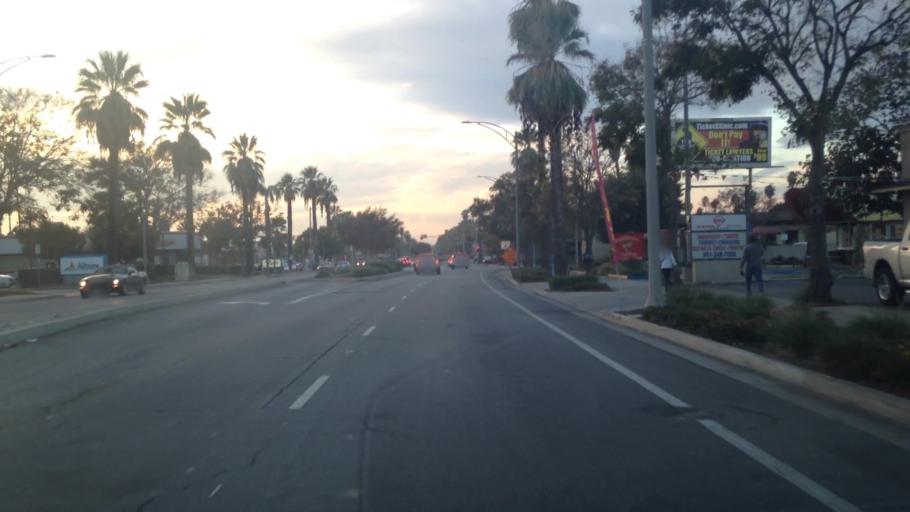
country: US
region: California
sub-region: Riverside County
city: Highgrove
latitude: 33.9758
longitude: -117.3462
